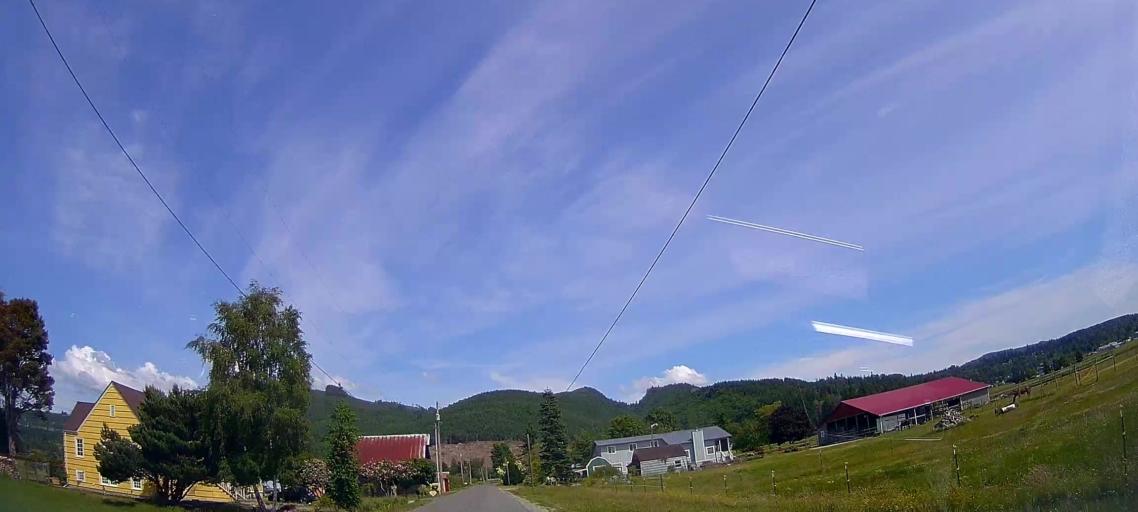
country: US
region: Washington
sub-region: Skagit County
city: Mount Vernon
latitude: 48.3595
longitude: -122.3265
